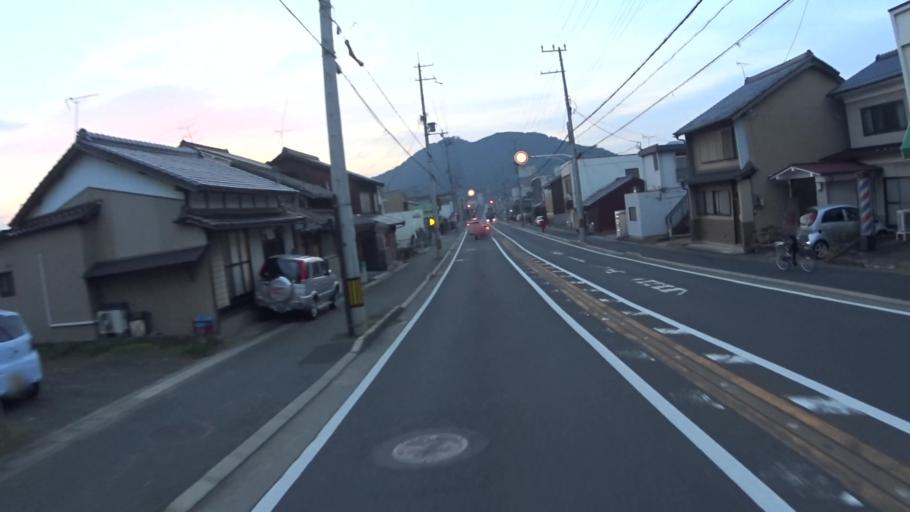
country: JP
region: Kyoto
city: Maizuru
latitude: 35.4451
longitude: 135.3356
